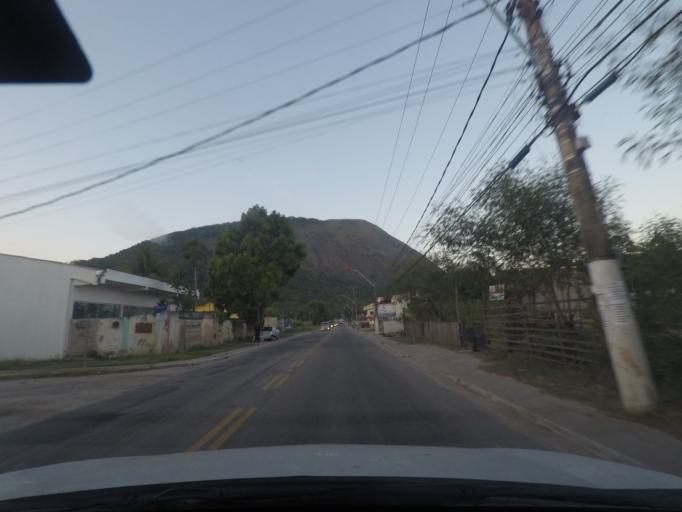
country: BR
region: Rio de Janeiro
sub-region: Marica
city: Marica
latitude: -22.9488
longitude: -42.9622
